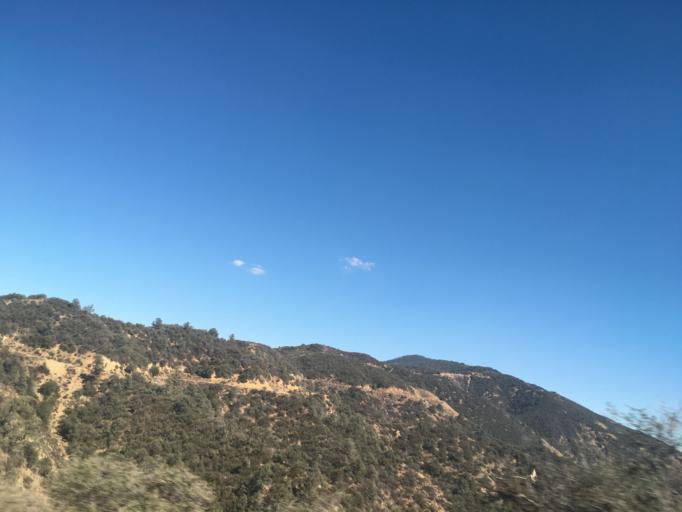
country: US
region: California
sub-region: Ventura County
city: Meiners Oaks
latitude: 34.6522
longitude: -119.3786
